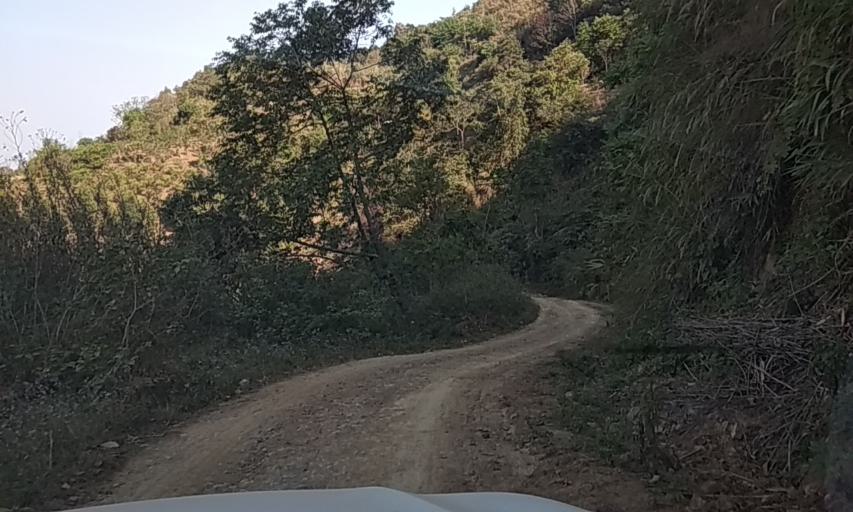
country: LA
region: Phongsali
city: Phongsali
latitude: 21.6901
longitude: 102.1014
